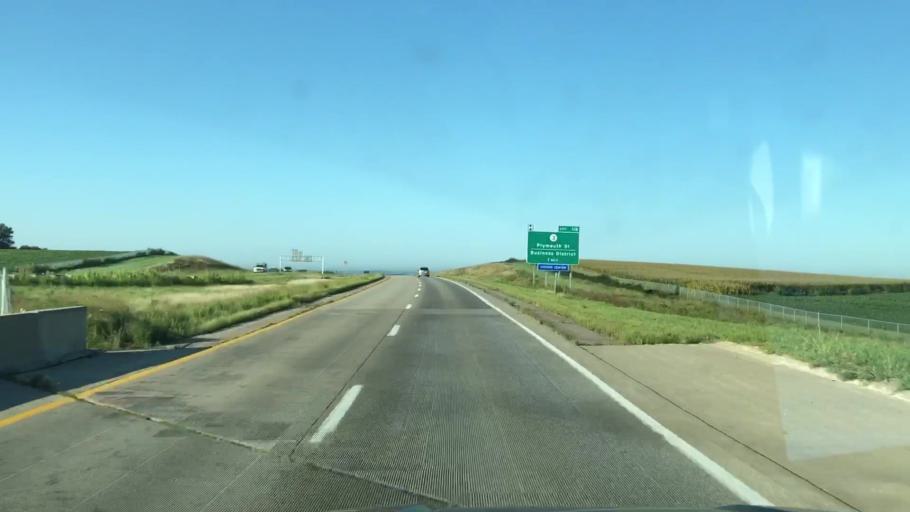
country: US
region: Iowa
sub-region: Plymouth County
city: Le Mars
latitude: 42.8119
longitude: -96.1944
